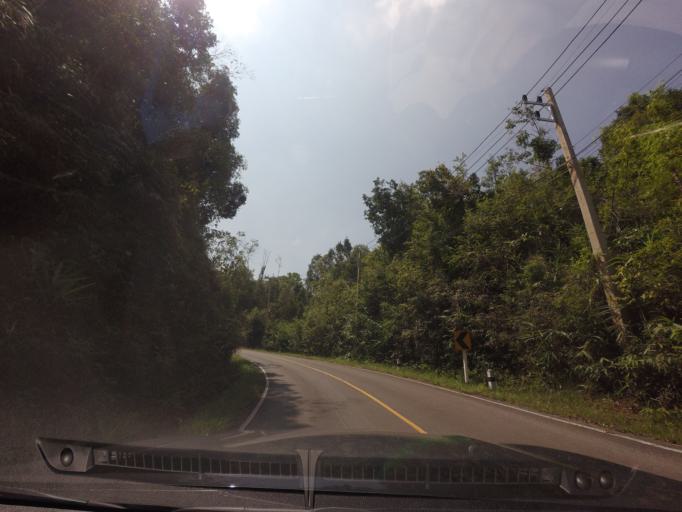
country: TH
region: Loei
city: Na Haeo
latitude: 17.4697
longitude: 100.9310
